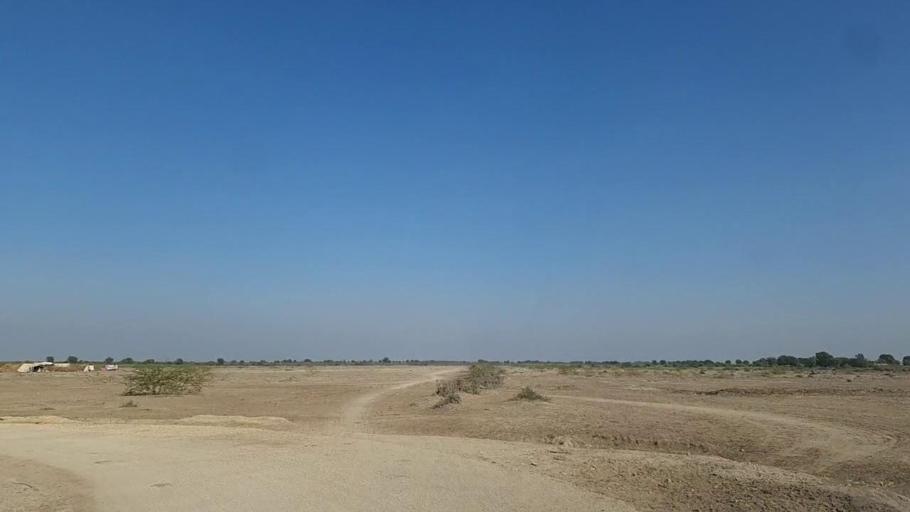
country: PK
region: Sindh
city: Samaro
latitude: 25.3525
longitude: 69.4402
